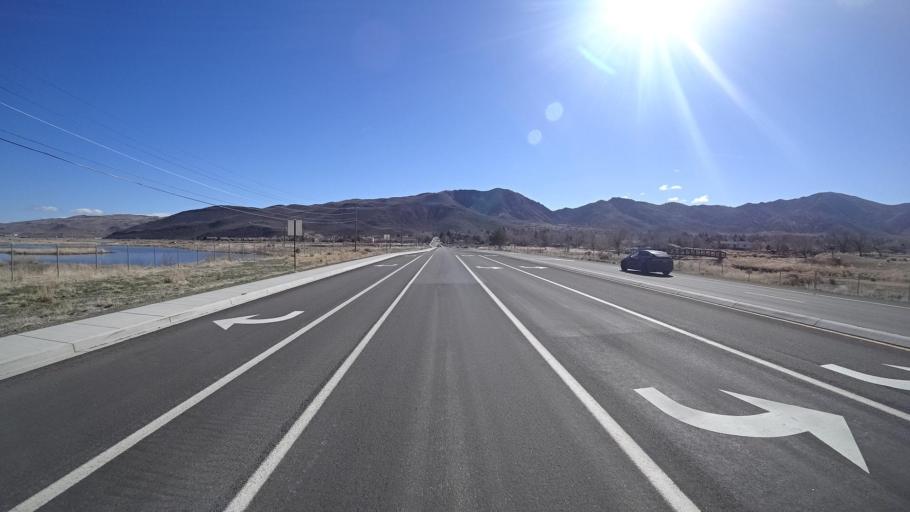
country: US
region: Nevada
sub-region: Washoe County
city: Sparks
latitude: 39.4981
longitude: -119.7280
